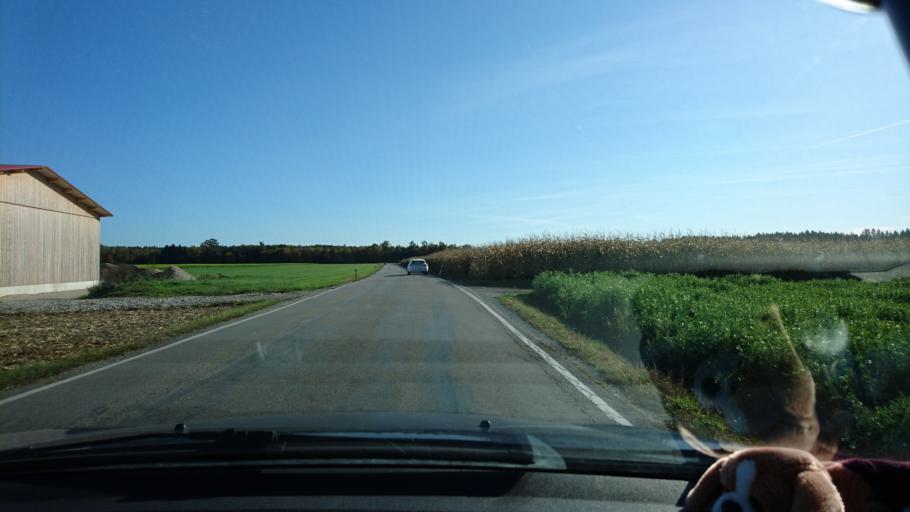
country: DE
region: Bavaria
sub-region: Upper Bavaria
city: Anzing
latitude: 48.1246
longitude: 11.8319
